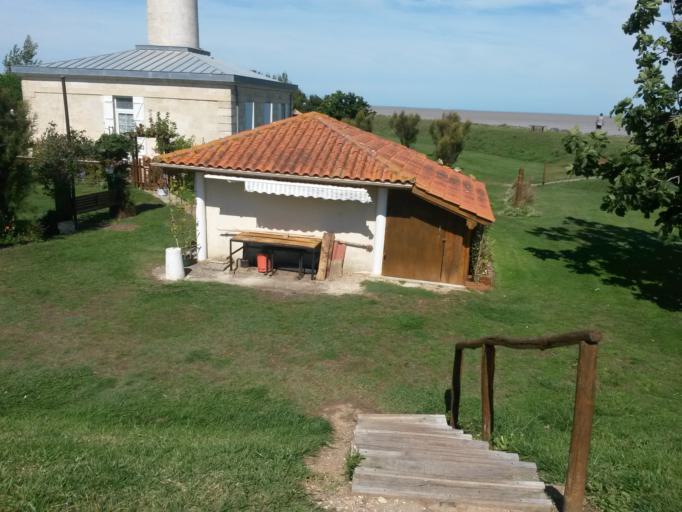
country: FR
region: Aquitaine
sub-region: Departement de la Gironde
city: Gaillan-en-Medoc
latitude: 45.4394
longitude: -0.9316
